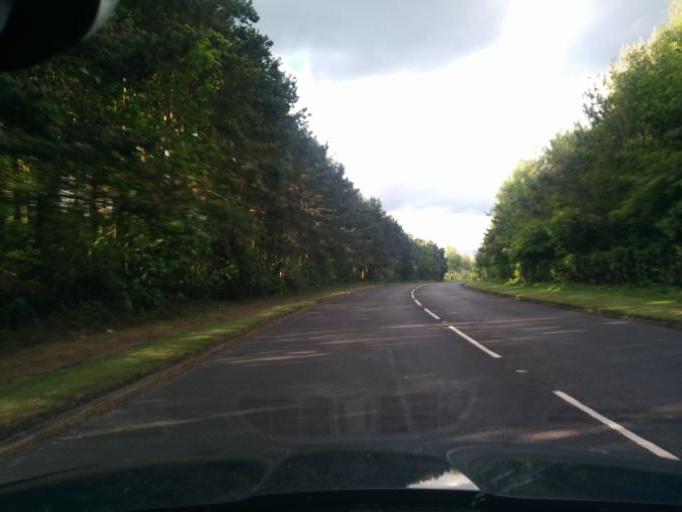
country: GB
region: England
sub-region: Northumberland
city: Bedlington
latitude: 55.1213
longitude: -1.6141
